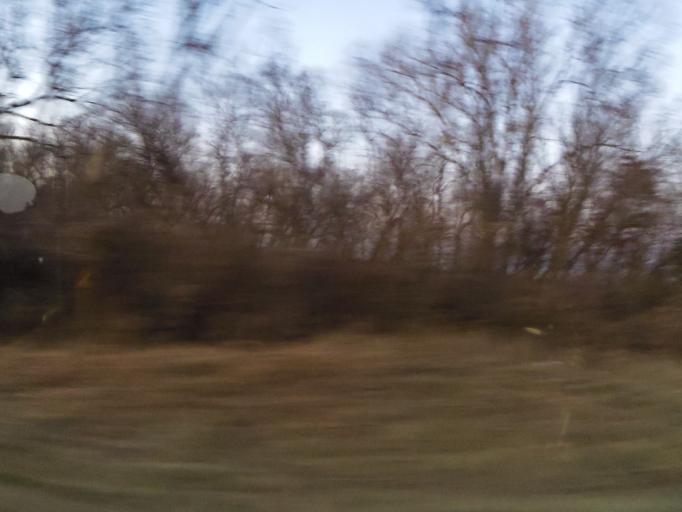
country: US
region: Wisconsin
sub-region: Pierce County
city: River Falls
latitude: 44.9132
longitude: -92.6769
